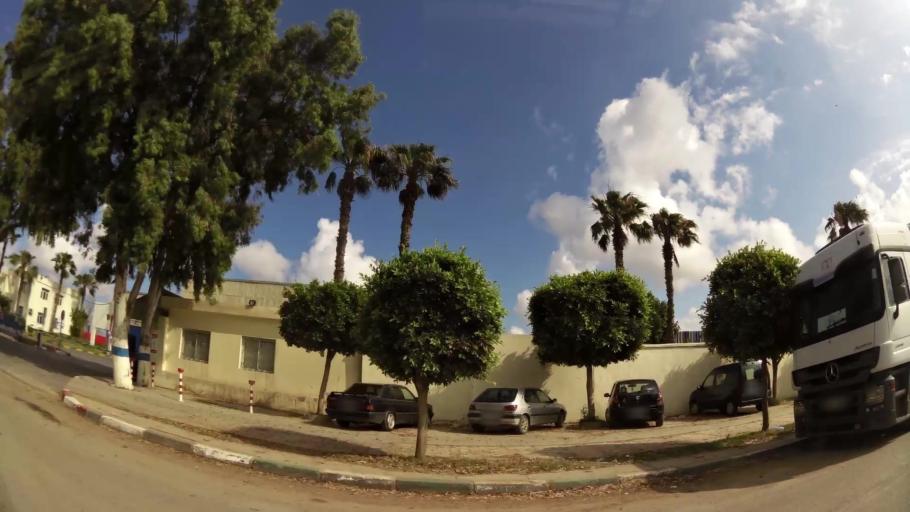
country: MA
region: Gharb-Chrarda-Beni Hssen
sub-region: Kenitra Province
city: Kenitra
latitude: 34.2780
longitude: -6.5485
